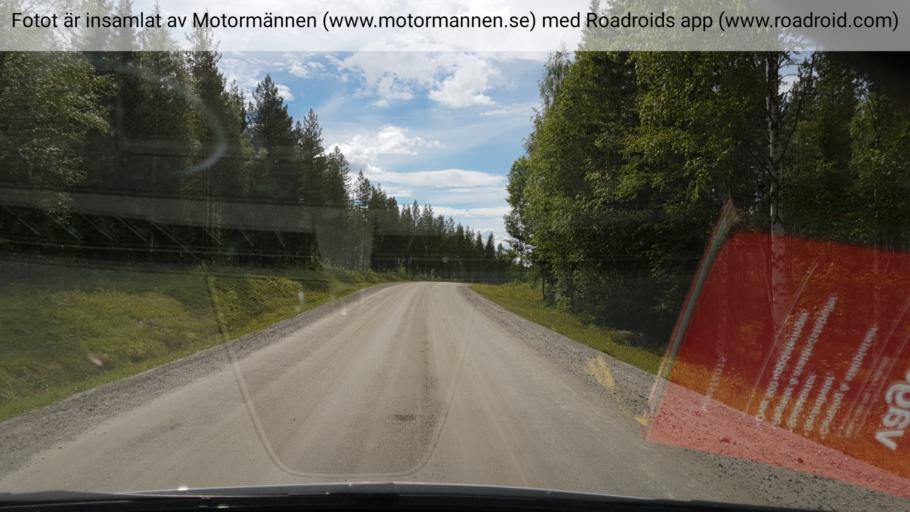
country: SE
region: Vaesternorrland
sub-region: Solleftea Kommun
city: Solleftea
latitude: 63.3192
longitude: 17.3196
